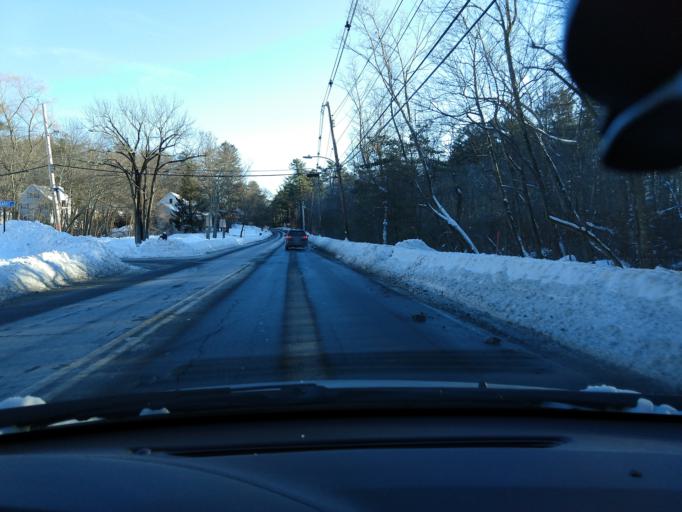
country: US
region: Massachusetts
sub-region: Middlesex County
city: Bedford
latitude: 42.4820
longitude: -71.2577
